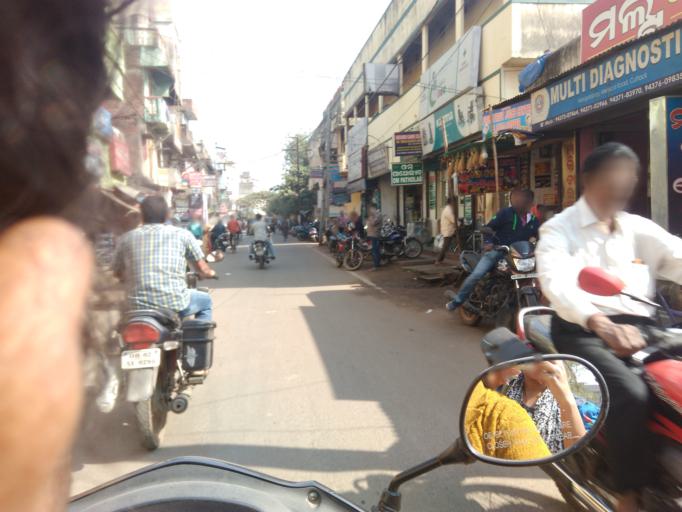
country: IN
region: Odisha
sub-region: Cuttack
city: Cuttack
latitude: 20.4729
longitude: 85.8862
